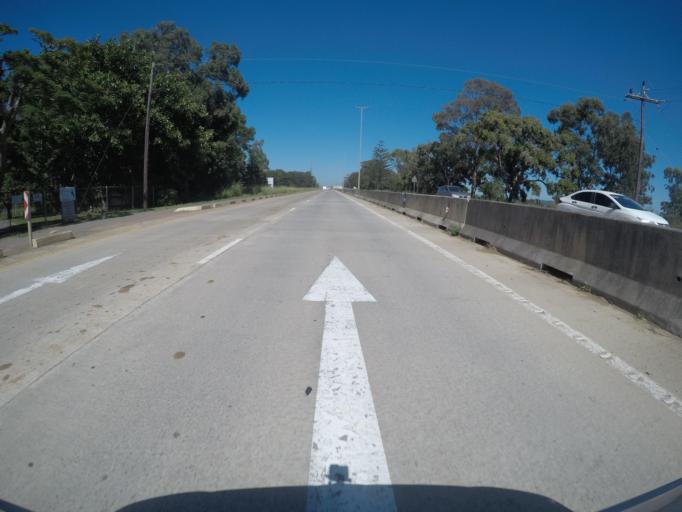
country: ZA
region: Eastern Cape
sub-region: Buffalo City Metropolitan Municipality
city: East London
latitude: -32.9380
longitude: 27.9811
